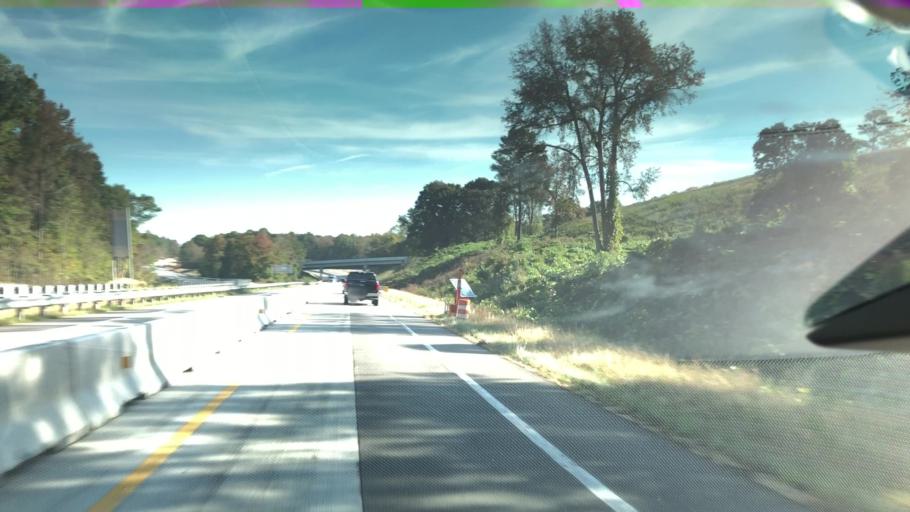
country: US
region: North Carolina
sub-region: Vance County
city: Henderson
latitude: 36.3675
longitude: -78.3652
